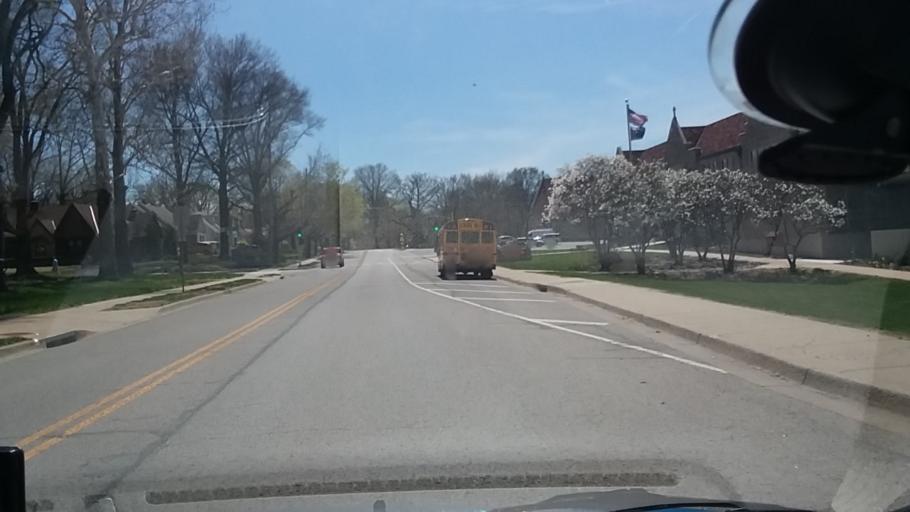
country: US
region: Kansas
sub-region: Johnson County
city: Westwood
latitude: 39.0353
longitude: -94.6212
